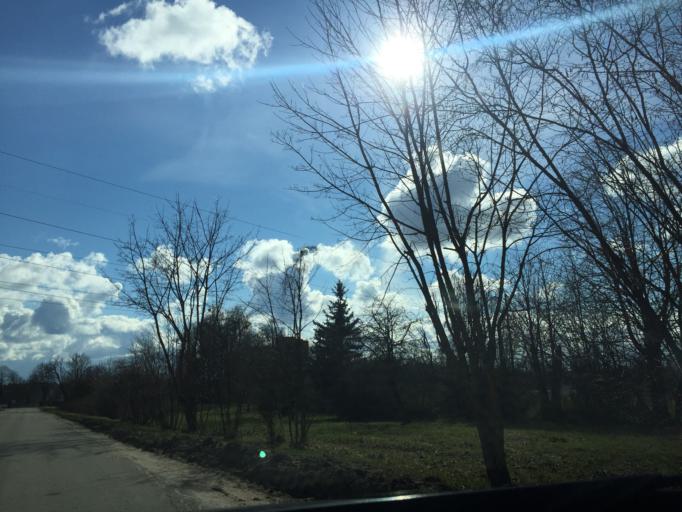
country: LV
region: Kekava
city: Kekava
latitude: 56.8288
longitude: 24.2311
